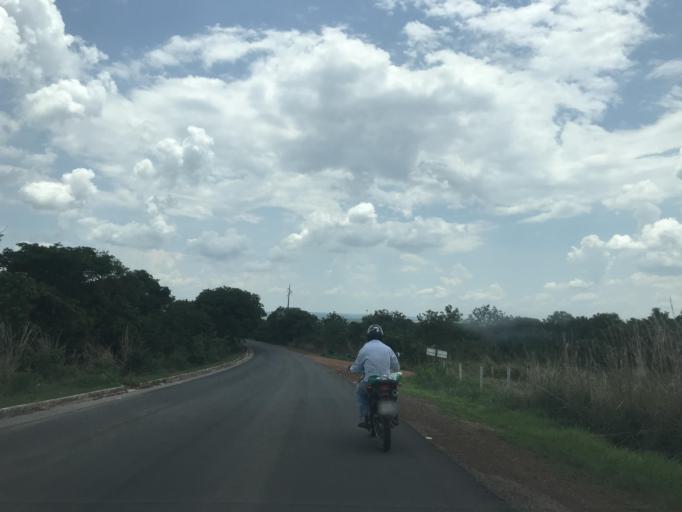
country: BR
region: Goias
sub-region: Bela Vista De Goias
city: Bela Vista de Goias
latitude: -17.0364
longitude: -48.6605
